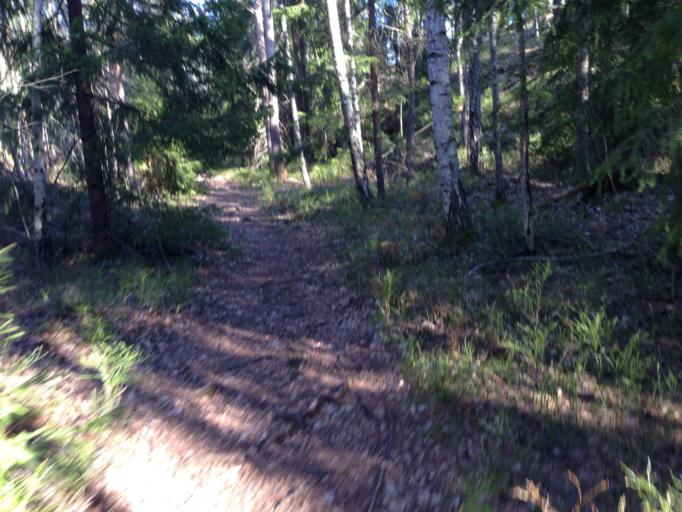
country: SE
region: Stockholm
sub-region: Nacka Kommun
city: Nacka
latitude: 59.2899
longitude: 18.1276
